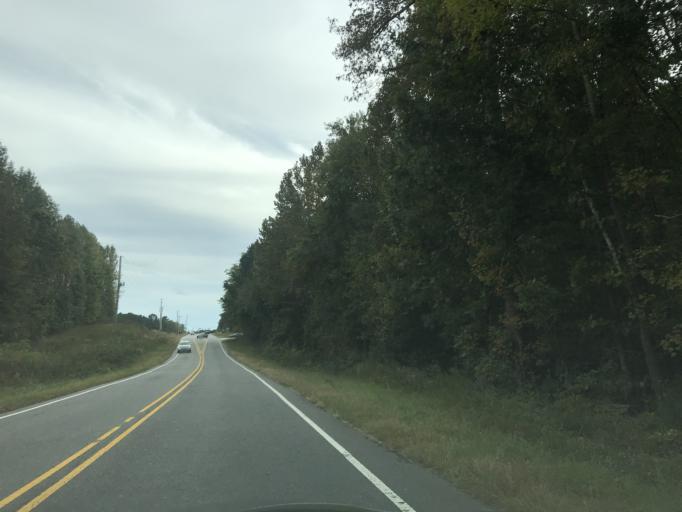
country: US
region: North Carolina
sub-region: Wake County
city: Rolesville
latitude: 35.9003
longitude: -78.5070
